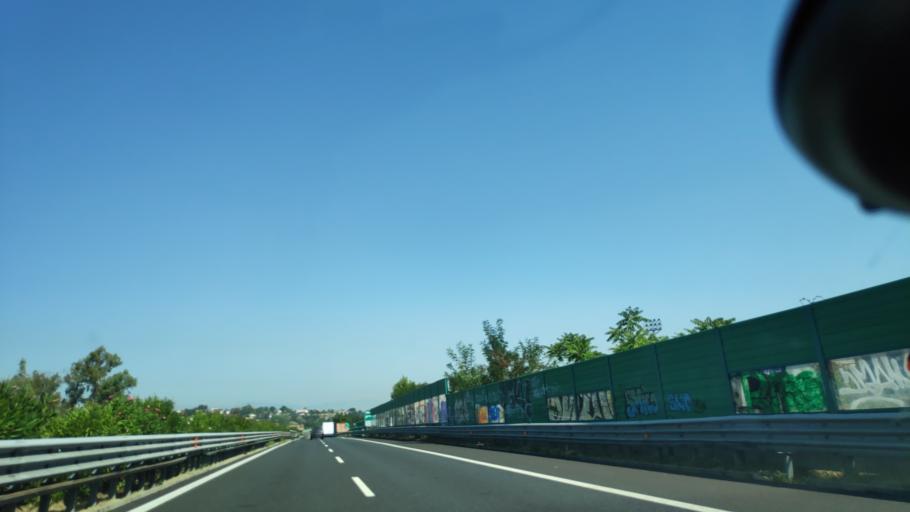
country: IT
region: Calabria
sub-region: Provincia di Cosenza
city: Quattromiglia
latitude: 39.3317
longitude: 16.2381
